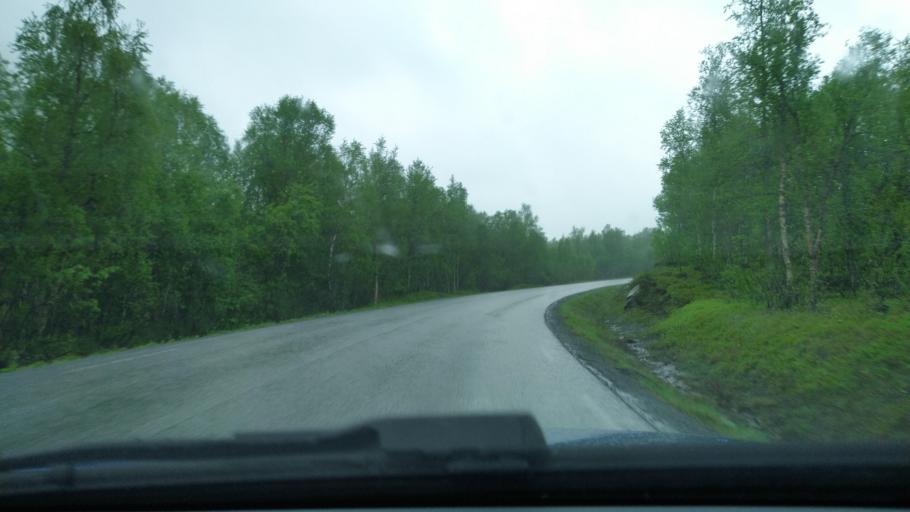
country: NO
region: Troms
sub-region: Dyroy
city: Brostadbotn
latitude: 69.0179
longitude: 17.7379
